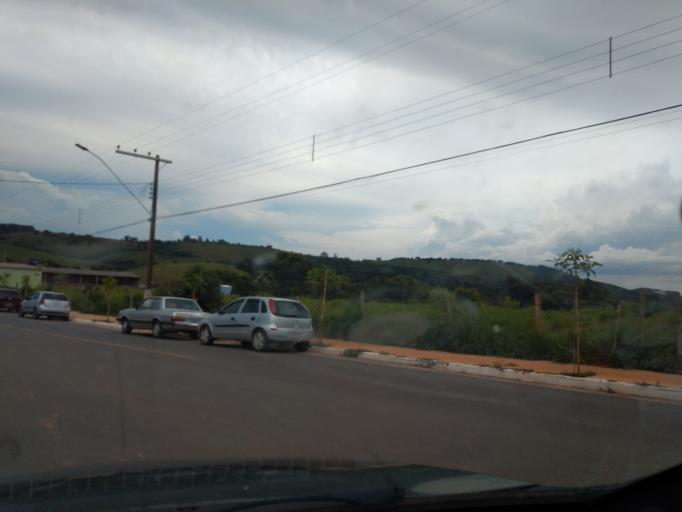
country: BR
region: Minas Gerais
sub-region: Lavras
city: Lavras
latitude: -21.5083
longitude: -44.9100
